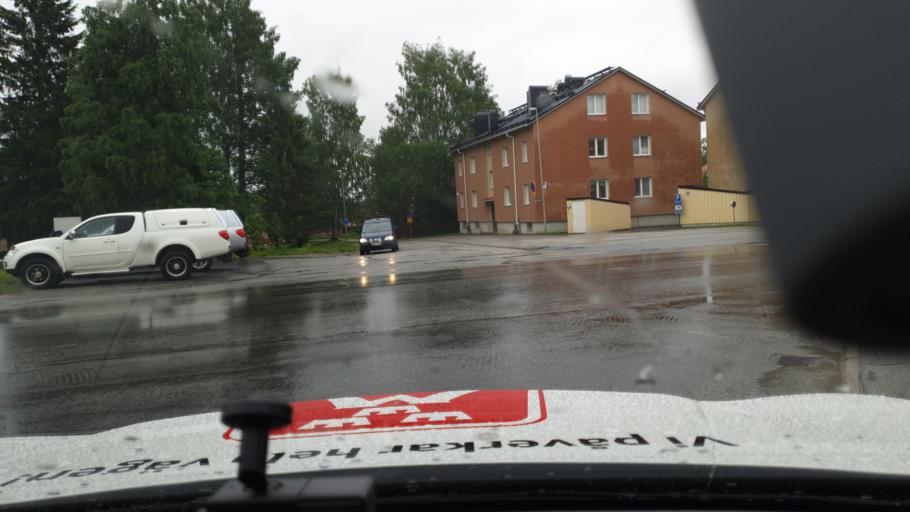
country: SE
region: Vaesterbotten
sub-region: Lycksele Kommun
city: Lycksele
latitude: 64.5995
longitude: 18.6687
